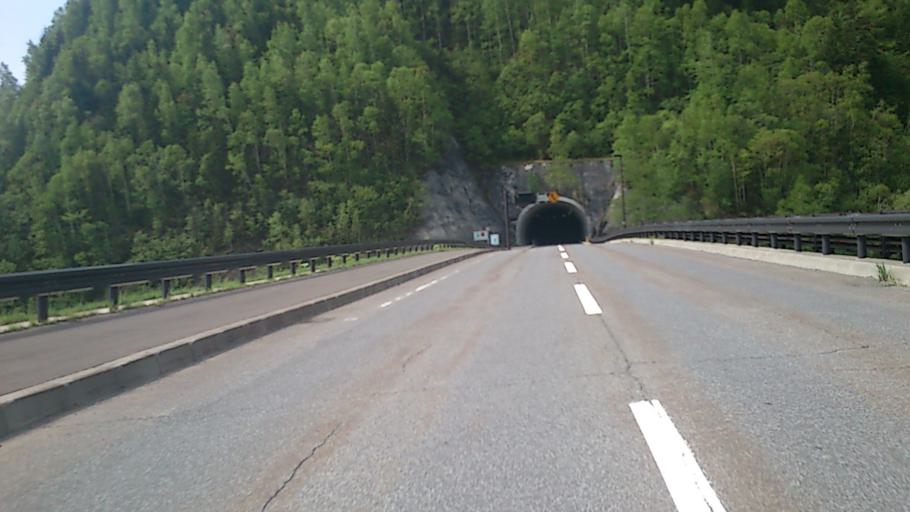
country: JP
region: Hokkaido
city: Kamikawa
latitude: 43.6758
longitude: 143.0363
